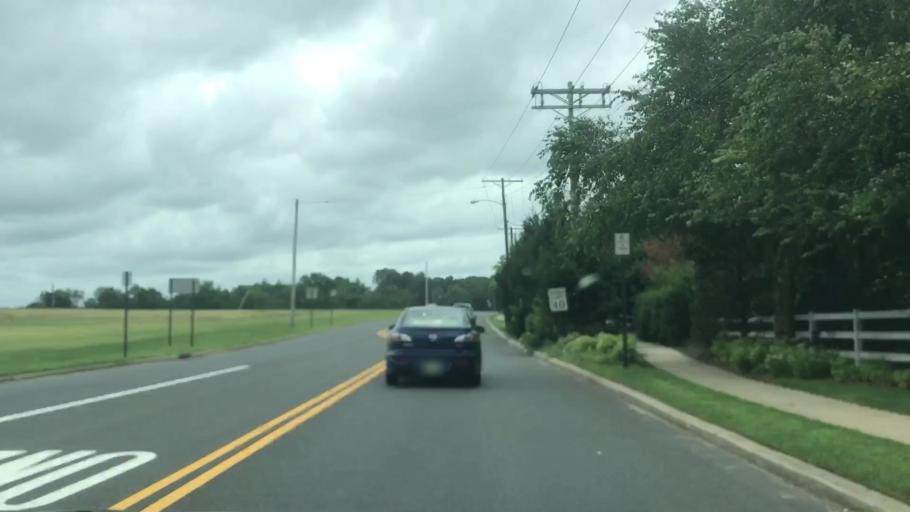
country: US
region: New Jersey
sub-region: Monmouth County
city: Oceanport
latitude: 40.3105
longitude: -74.0233
